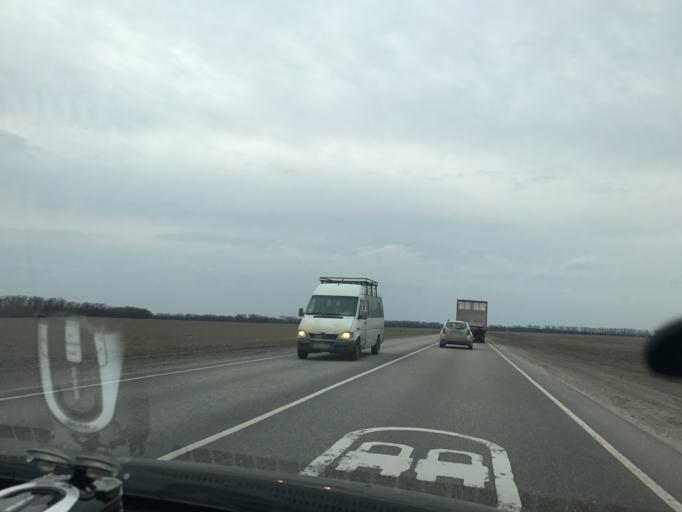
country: RU
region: Krasnodarskiy
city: Alekseyevskaya
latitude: 45.7686
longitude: 40.2395
